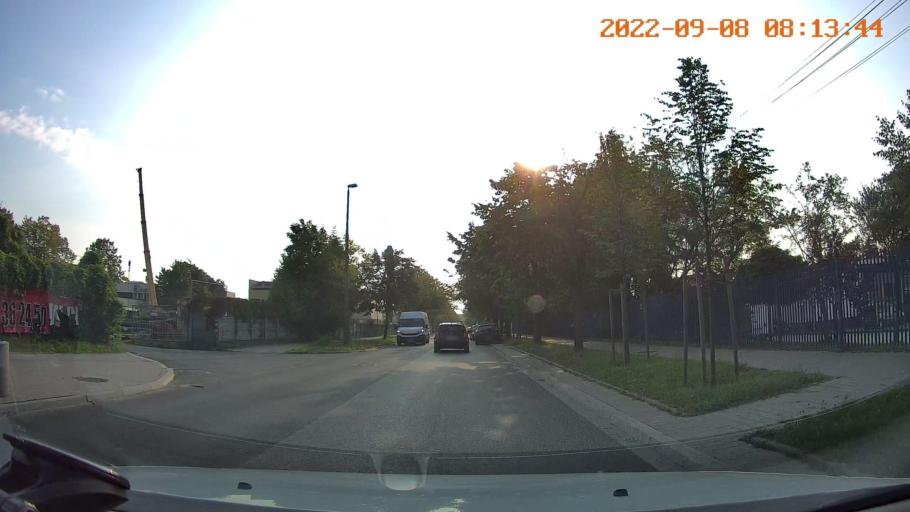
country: PL
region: Lesser Poland Voivodeship
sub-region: Powiat krakowski
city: Rzaska
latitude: 50.0794
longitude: 19.8722
